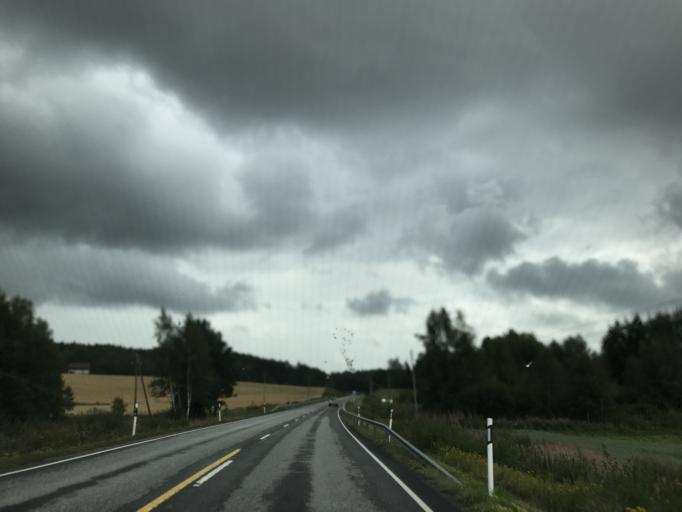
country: FI
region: Varsinais-Suomi
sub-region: Salo
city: Pernioe
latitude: 60.0900
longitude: 23.2268
